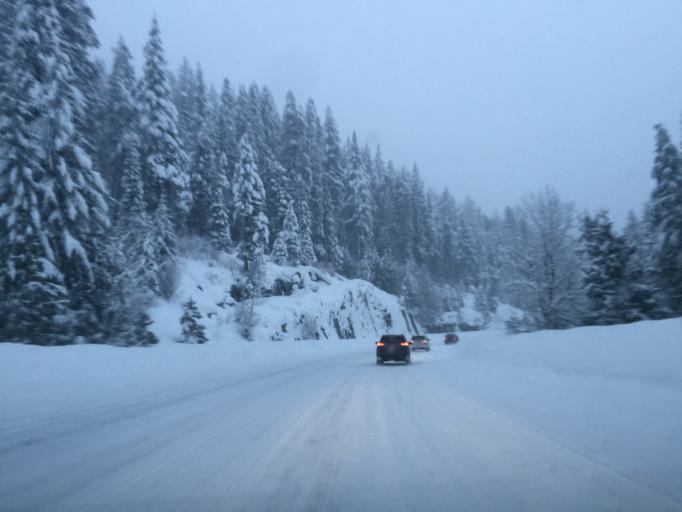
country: US
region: Washington
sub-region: Chelan County
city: Leavenworth
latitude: 47.7873
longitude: -120.8912
